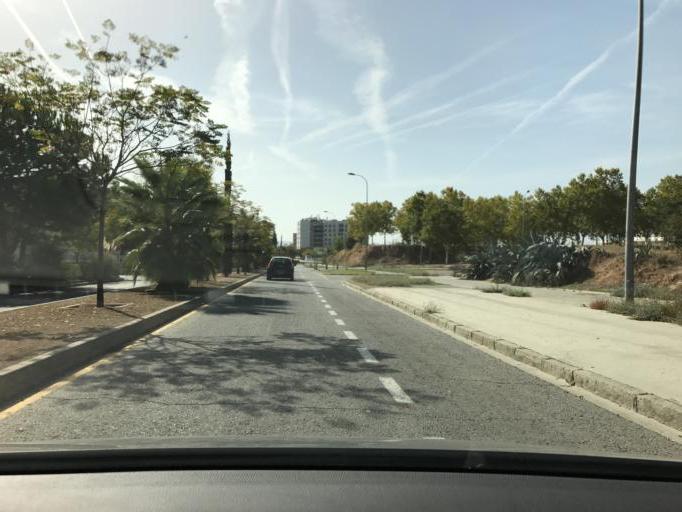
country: ES
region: Andalusia
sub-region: Provincia de Granada
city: Granada
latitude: 37.2045
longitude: -3.6144
